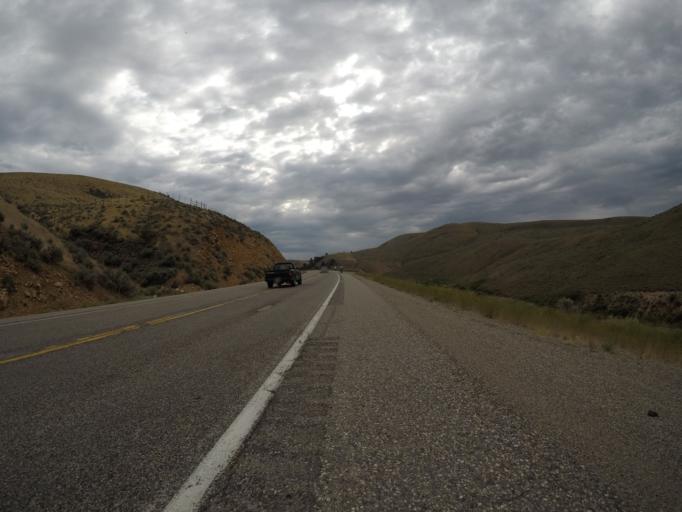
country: US
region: Wyoming
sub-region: Lincoln County
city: Kemmerer
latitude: 41.8228
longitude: -110.8615
